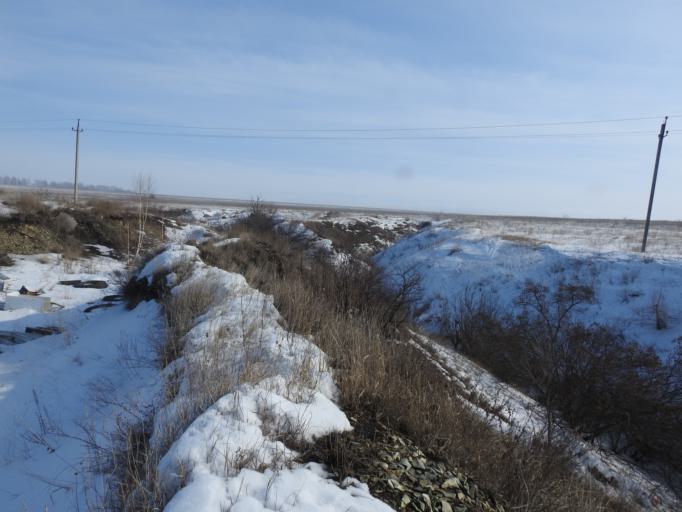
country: RU
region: Saratov
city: Sokolovyy
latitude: 51.5116
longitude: 45.7911
